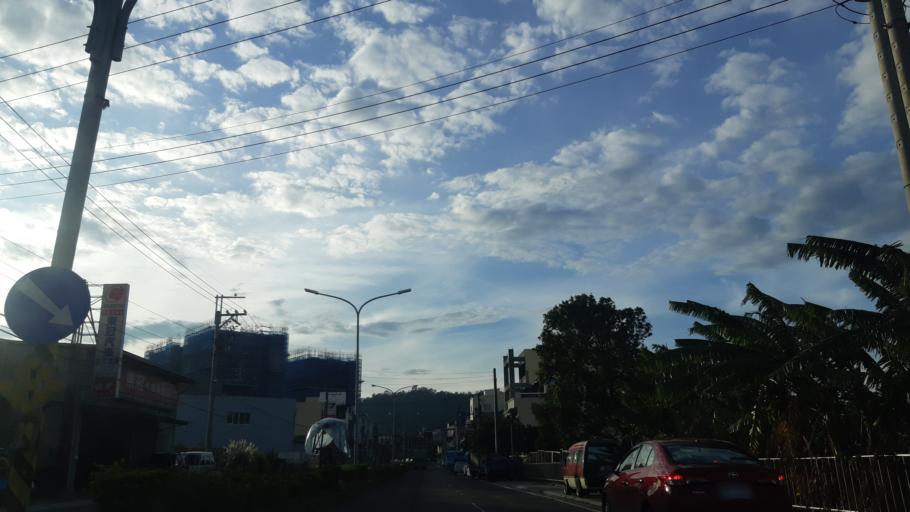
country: TW
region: Taiwan
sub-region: Hsinchu
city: Zhubei
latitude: 24.7306
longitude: 121.0972
